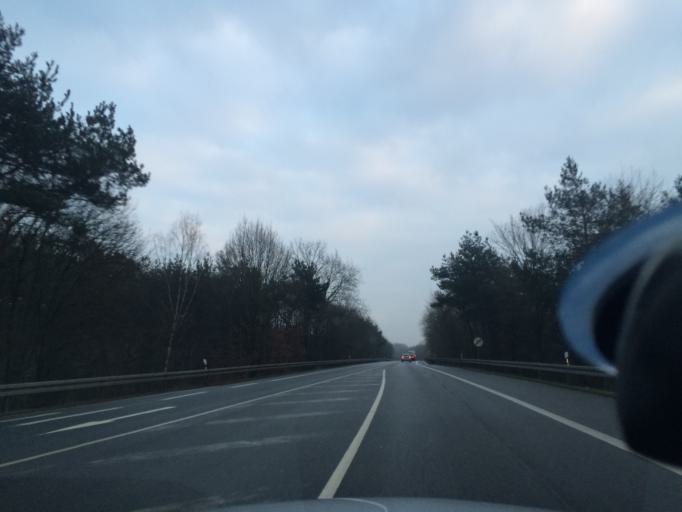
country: DE
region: Hesse
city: Morfelden-Walldorf
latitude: 50.0331
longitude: 8.6003
